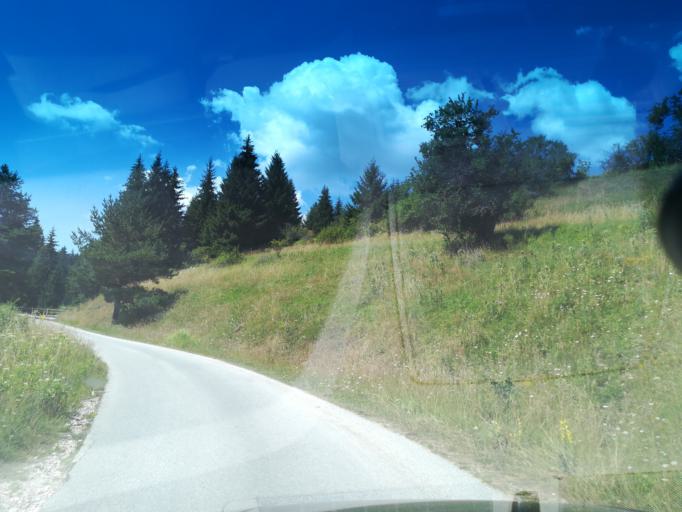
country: BG
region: Smolyan
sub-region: Obshtina Chepelare
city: Chepelare
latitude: 41.6707
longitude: 24.7897
